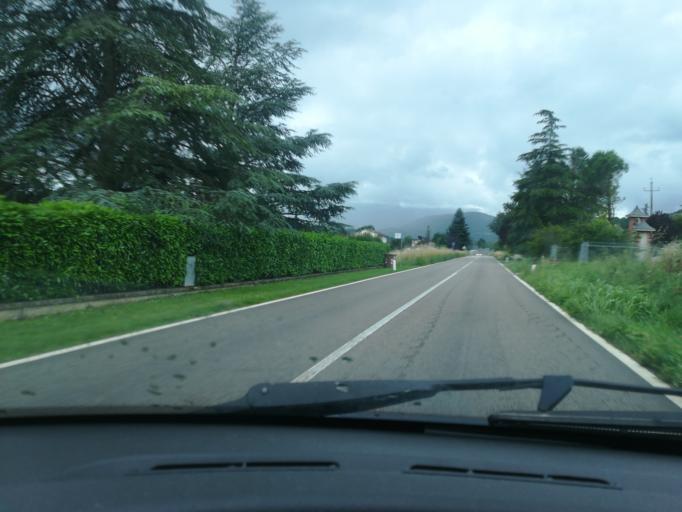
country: IT
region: The Marches
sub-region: Provincia di Macerata
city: San Ginesio
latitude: 43.0919
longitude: 13.3172
